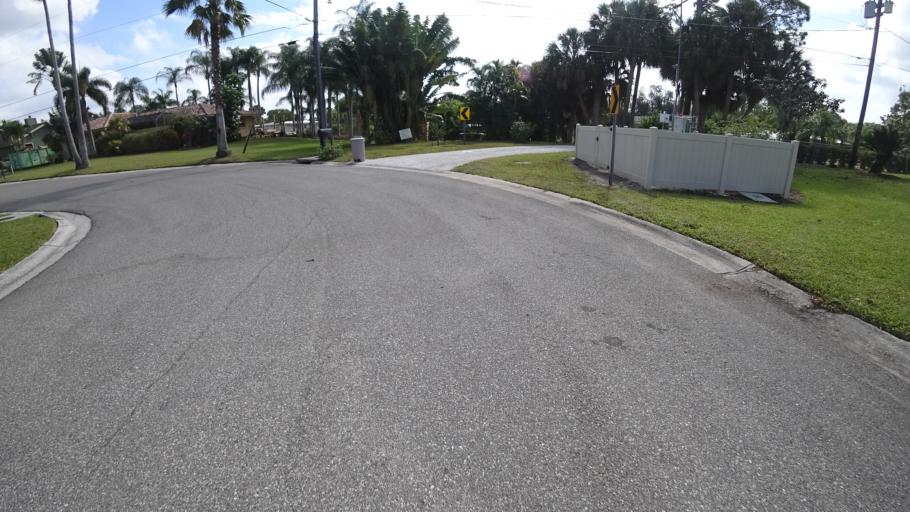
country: US
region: Florida
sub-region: Manatee County
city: Whitfield
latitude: 27.4193
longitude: -82.5660
